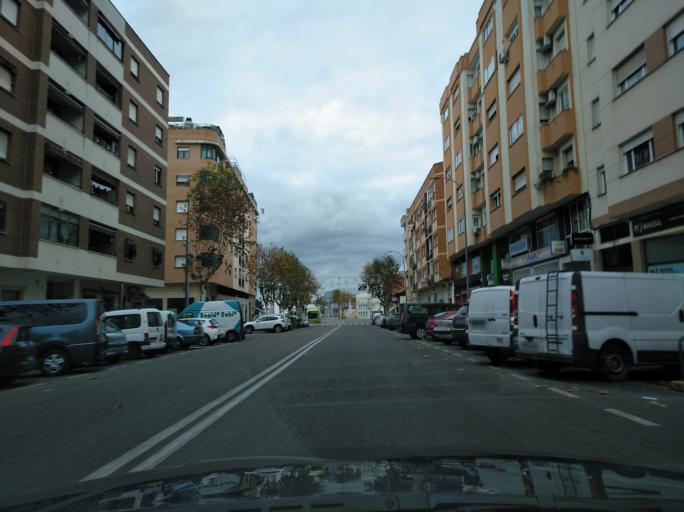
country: ES
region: Extremadura
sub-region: Provincia de Badajoz
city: Badajoz
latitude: 38.8786
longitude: -6.9520
